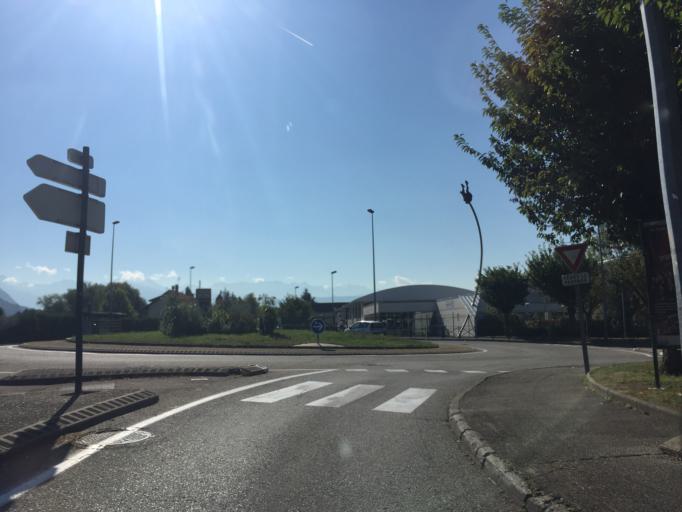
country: FR
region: Rhone-Alpes
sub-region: Departement de la Savoie
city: La Ravoire
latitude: 45.5517
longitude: 5.9692
